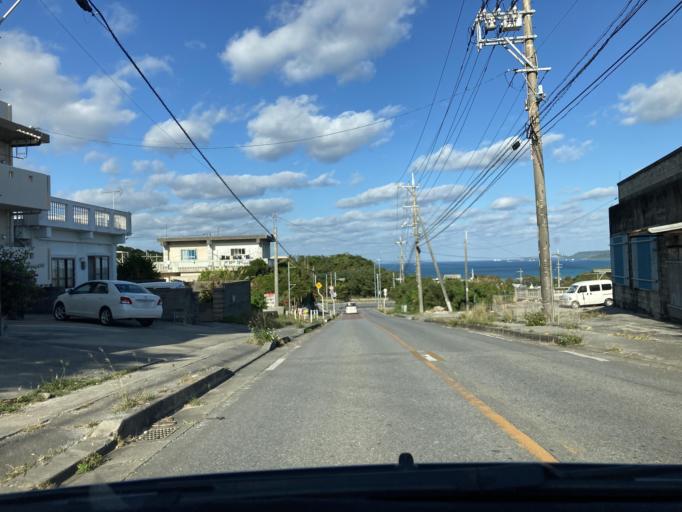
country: JP
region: Okinawa
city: Katsuren-haebaru
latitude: 26.3275
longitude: 127.8937
